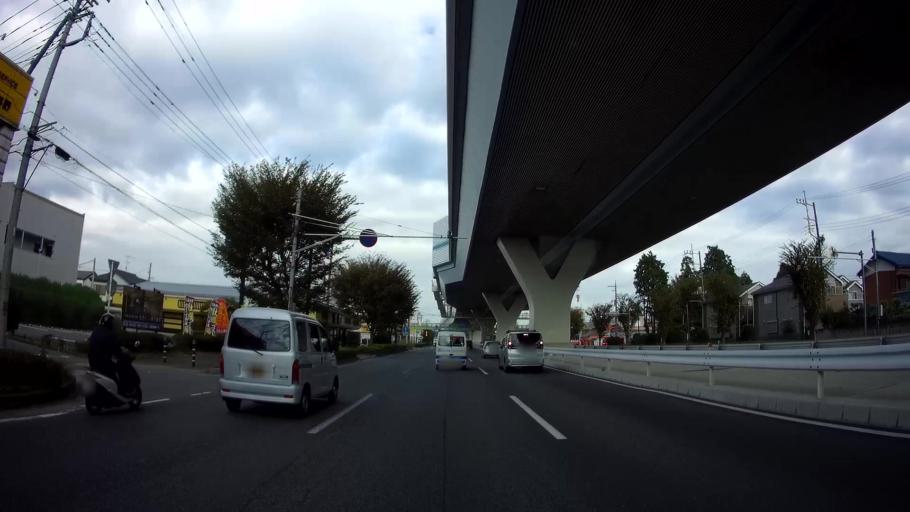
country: JP
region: Saitama
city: Yono
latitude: 35.8819
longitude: 139.6163
